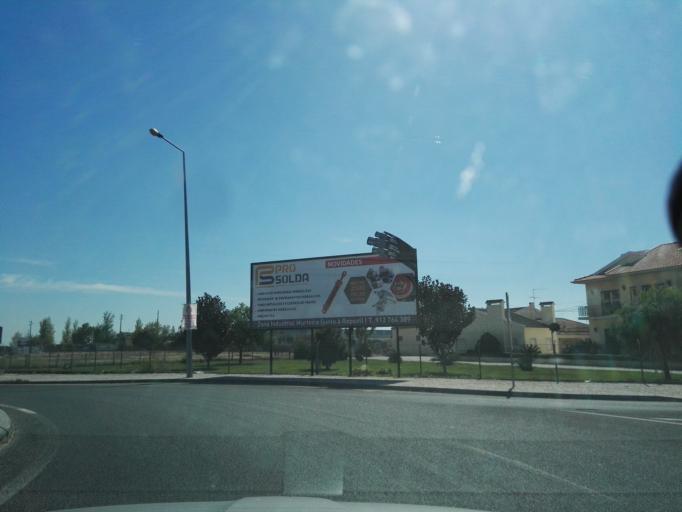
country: PT
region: Santarem
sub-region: Benavente
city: Samora Correia
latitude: 38.9201
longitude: -8.8774
